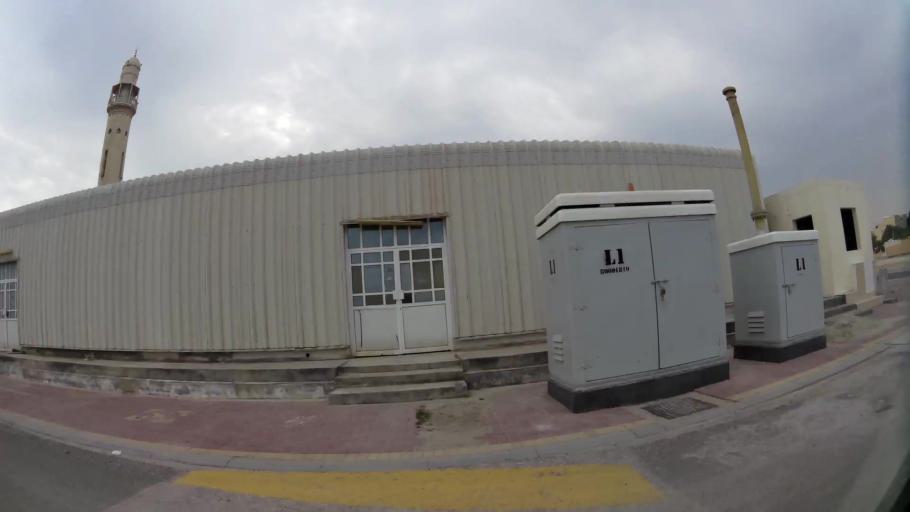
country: BH
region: Northern
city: Ar Rifa'
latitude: 26.0561
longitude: 50.6195
